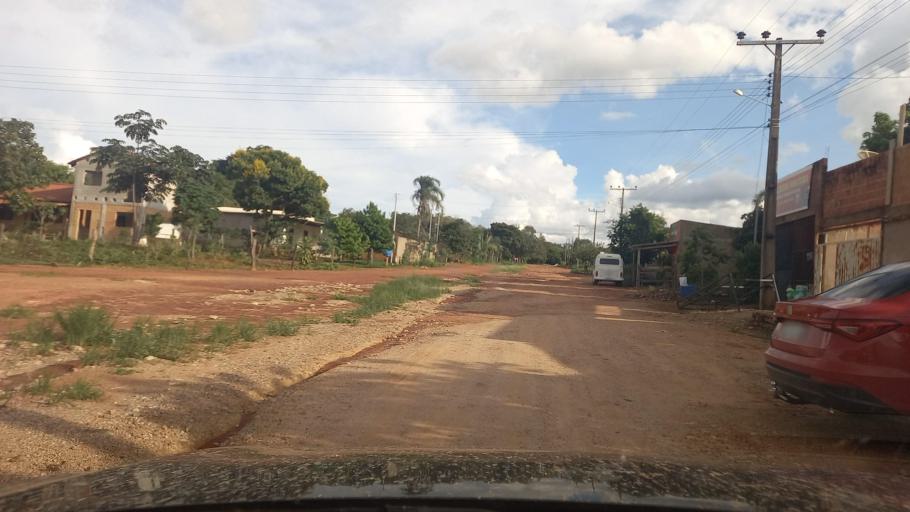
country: BR
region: Goias
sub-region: Cavalcante
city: Cavalcante
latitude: -13.7974
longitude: -47.4414
